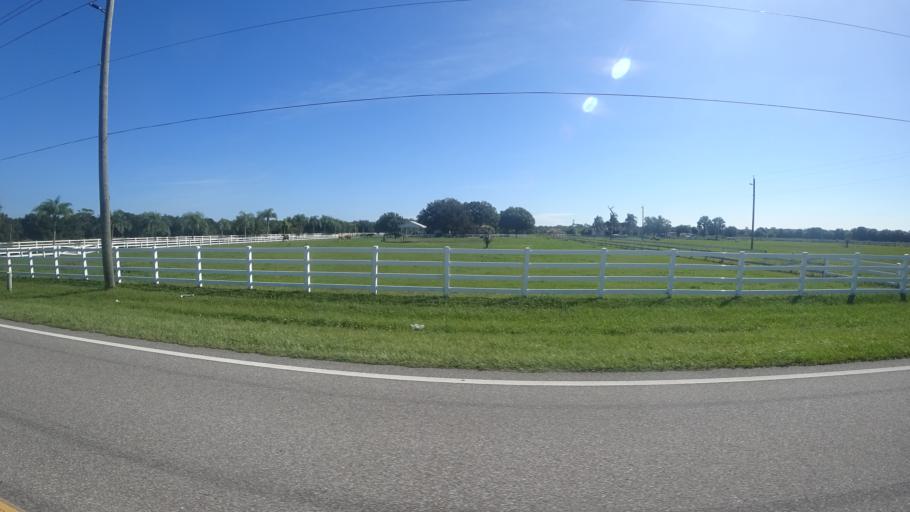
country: US
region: Florida
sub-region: Sarasota County
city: Lake Sarasota
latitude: 27.3640
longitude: -82.2684
